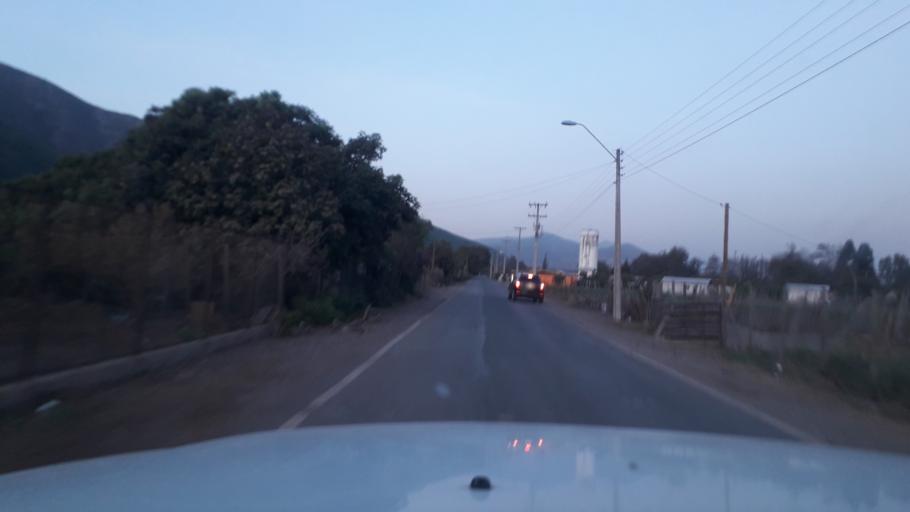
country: CL
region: Valparaiso
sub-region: Provincia de San Felipe
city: Llaillay
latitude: -32.8255
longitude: -71.0286
